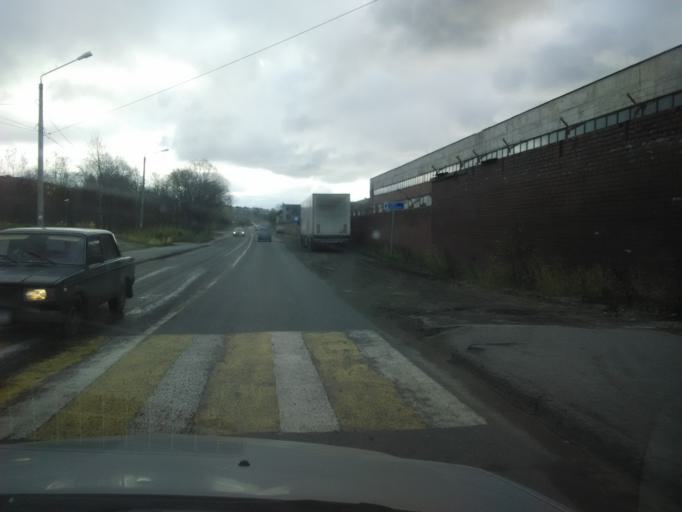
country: RU
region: Murmansk
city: Kandalaksha
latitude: 67.1560
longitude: 32.4016
